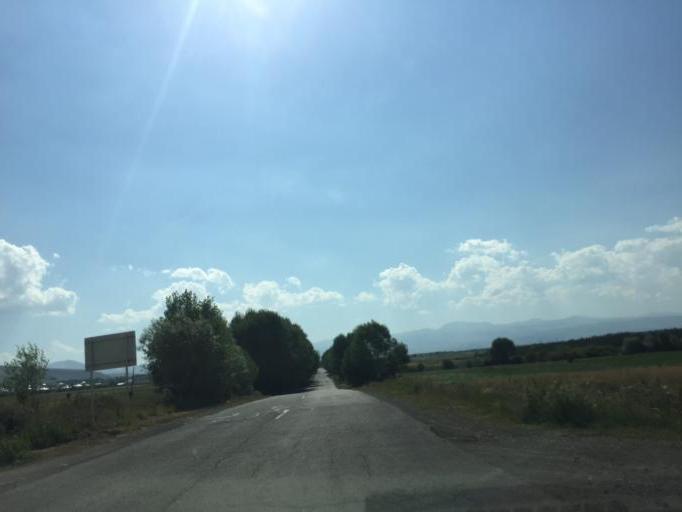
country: AM
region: Geghark'unik'i Marz
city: Astghadzor
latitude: 40.1445
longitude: 45.3863
